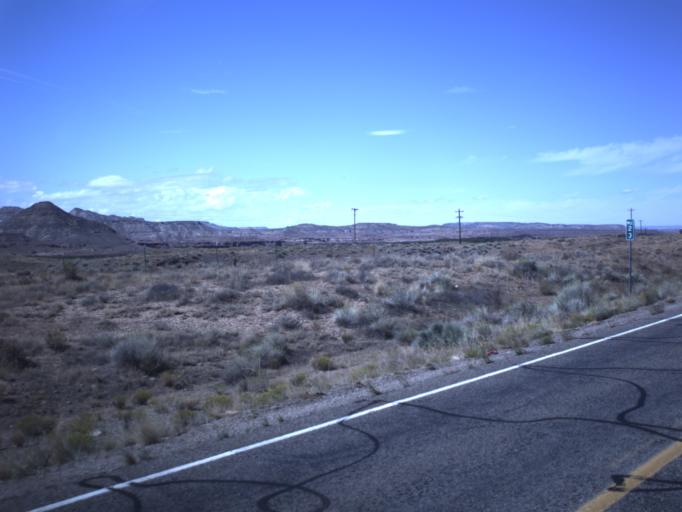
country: US
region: Colorado
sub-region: Montezuma County
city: Towaoc
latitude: 37.2121
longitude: -109.1747
